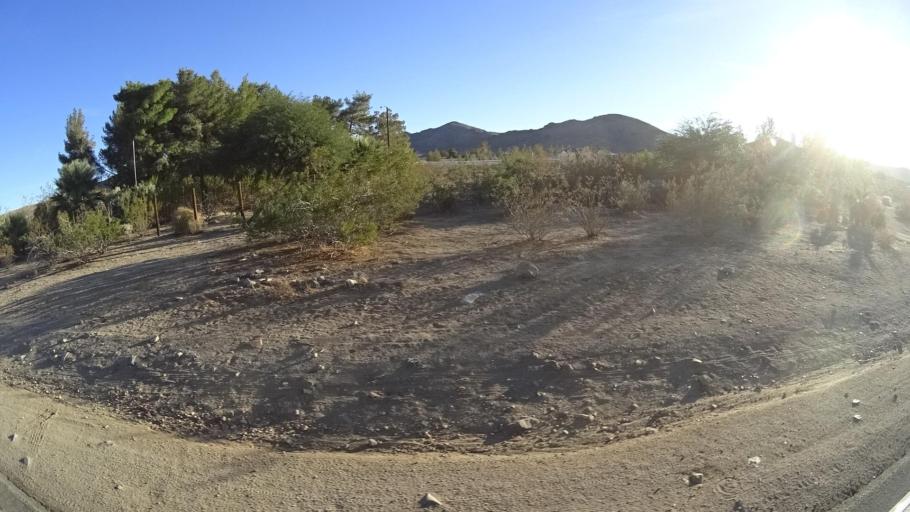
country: US
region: California
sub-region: Kern County
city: Ridgecrest
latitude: 35.5860
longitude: -117.6538
